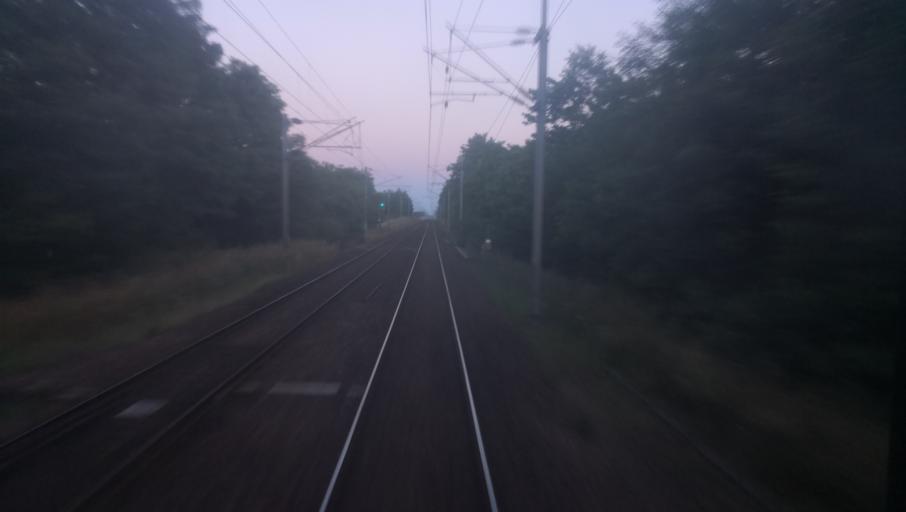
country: FR
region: Centre
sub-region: Departement du Loiret
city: Briare
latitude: 47.6080
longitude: 2.7790
